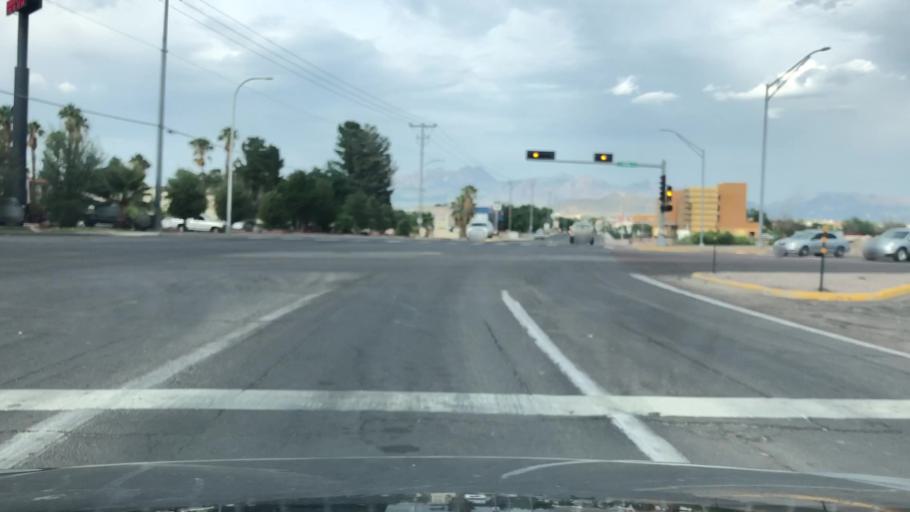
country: US
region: New Mexico
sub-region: Dona Ana County
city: University Park
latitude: 32.2818
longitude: -106.7682
